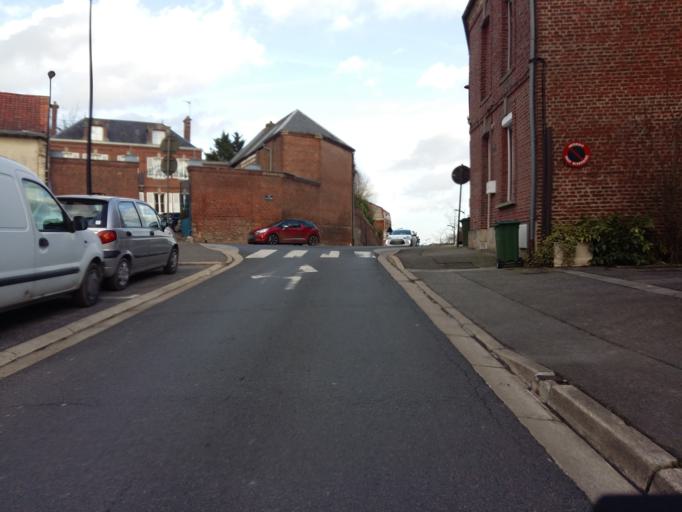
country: FR
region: Picardie
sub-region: Departement de la Somme
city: Camon
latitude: 49.8855
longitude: 2.3481
